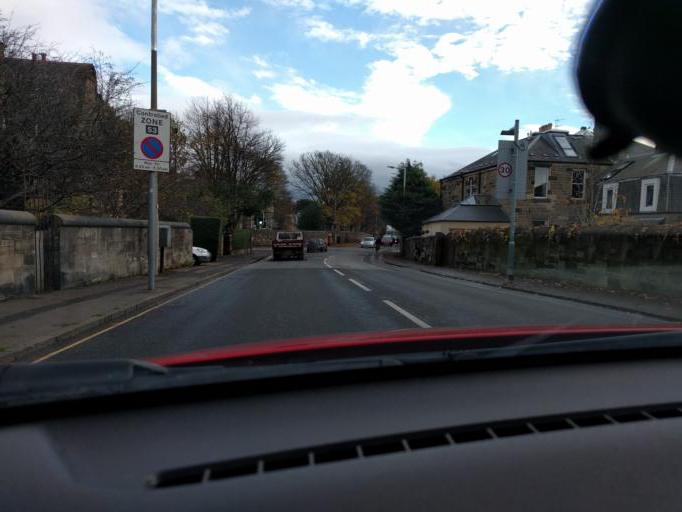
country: GB
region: Scotland
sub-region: Edinburgh
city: Edinburgh
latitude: 55.9314
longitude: -3.2267
